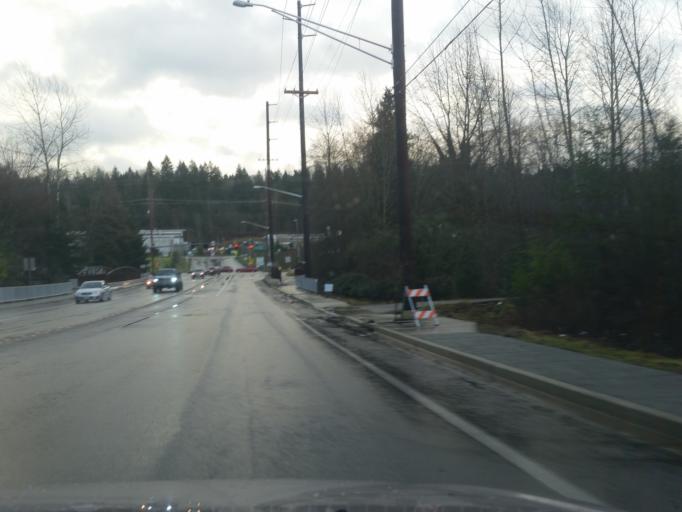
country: US
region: Washington
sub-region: Snohomish County
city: Maltby
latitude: 47.7904
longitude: -122.1455
